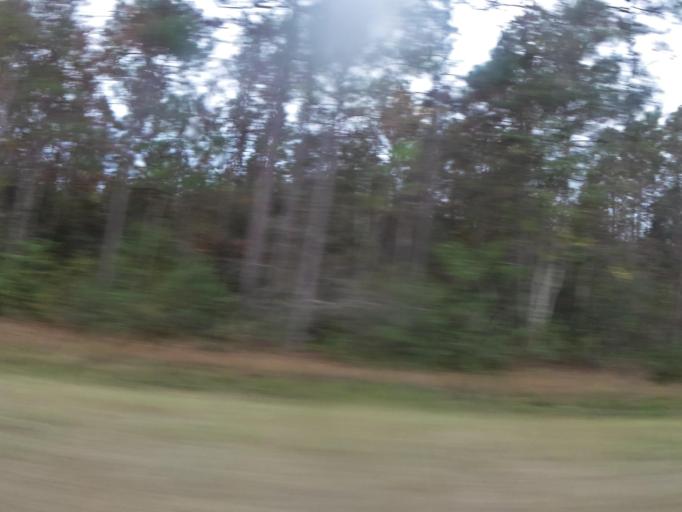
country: US
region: Georgia
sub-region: Charlton County
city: Folkston
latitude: 30.8890
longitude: -82.0466
